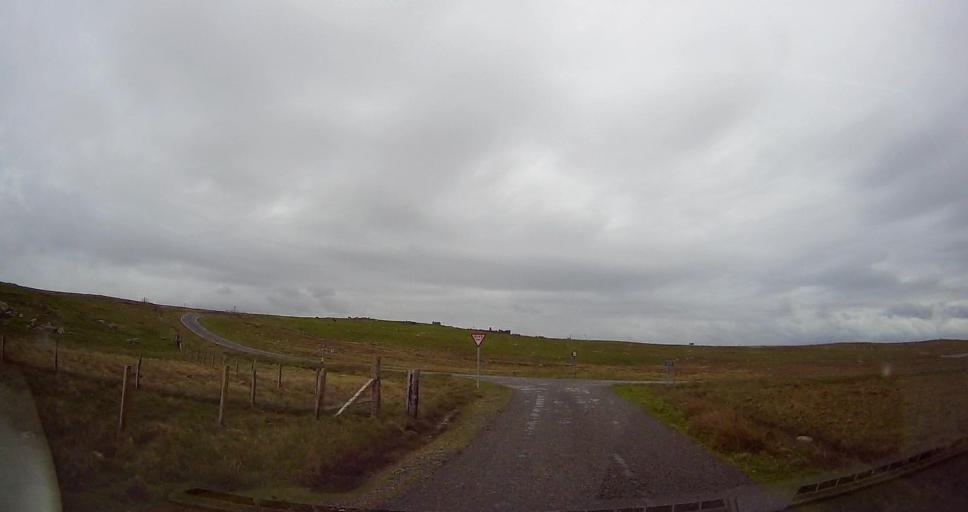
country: GB
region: Scotland
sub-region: Shetland Islands
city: Lerwick
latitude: 60.4852
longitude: -1.6083
